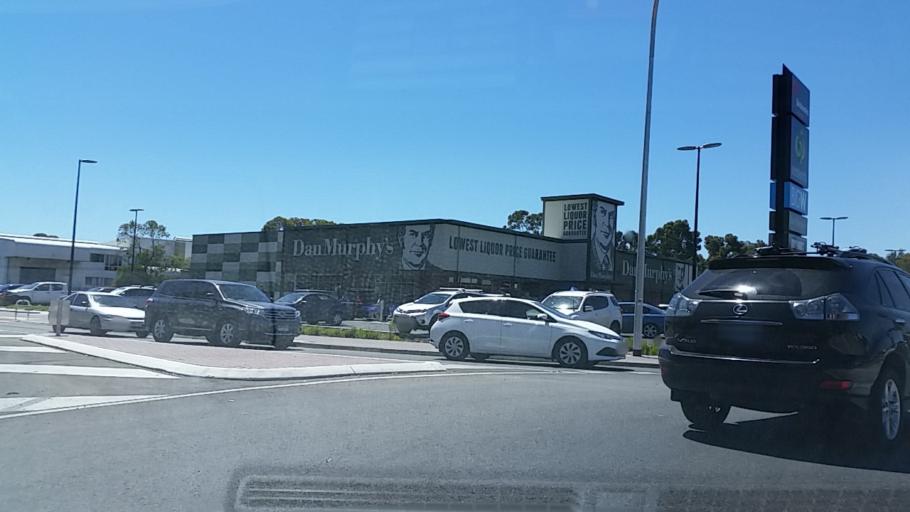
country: AU
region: South Australia
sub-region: City of West Torrens
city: Thebarton
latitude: -34.9145
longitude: 138.5628
